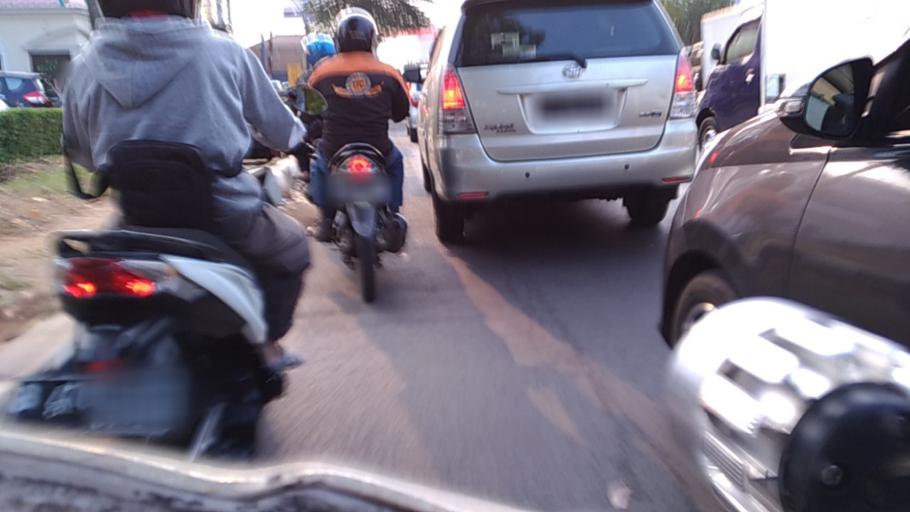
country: ID
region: West Java
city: Cileungsir
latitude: -6.3777
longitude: 106.9200
